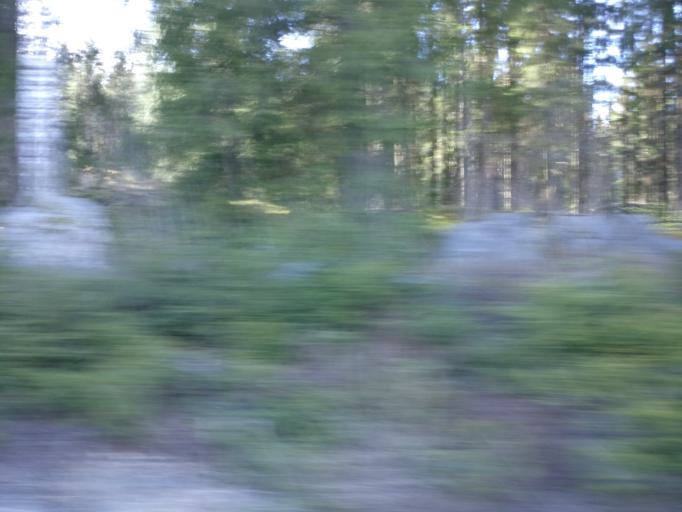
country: FI
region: Varsinais-Suomi
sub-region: Salo
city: Suomusjaervi
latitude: 60.3142
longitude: 23.6444
